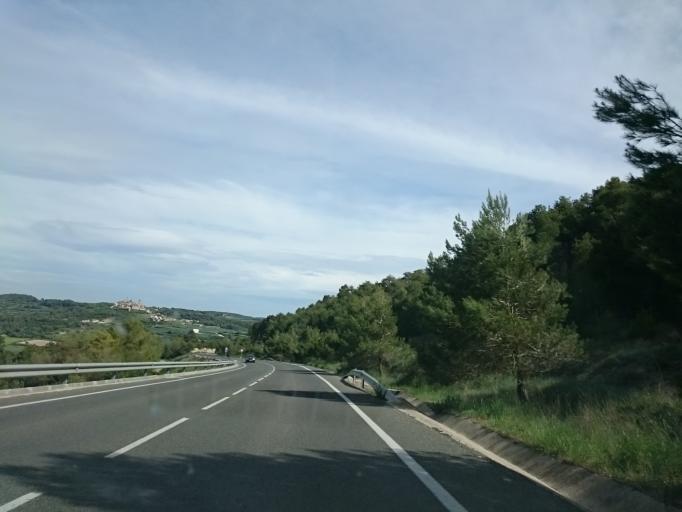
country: ES
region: Catalonia
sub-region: Provincia de Tarragona
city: Santa Coloma de Queralt
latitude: 41.5596
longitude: 1.4009
